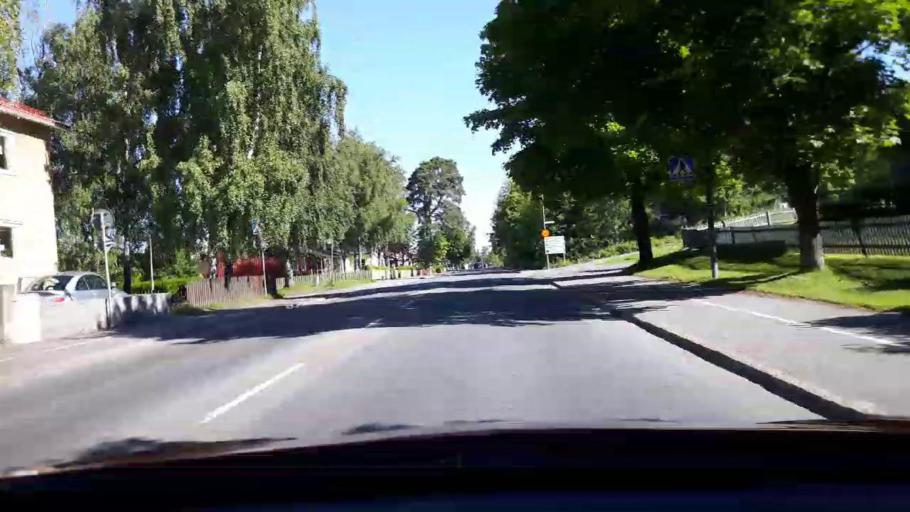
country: SE
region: Jaemtland
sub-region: OEstersunds Kommun
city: Ostersund
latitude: 63.1848
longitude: 14.6539
